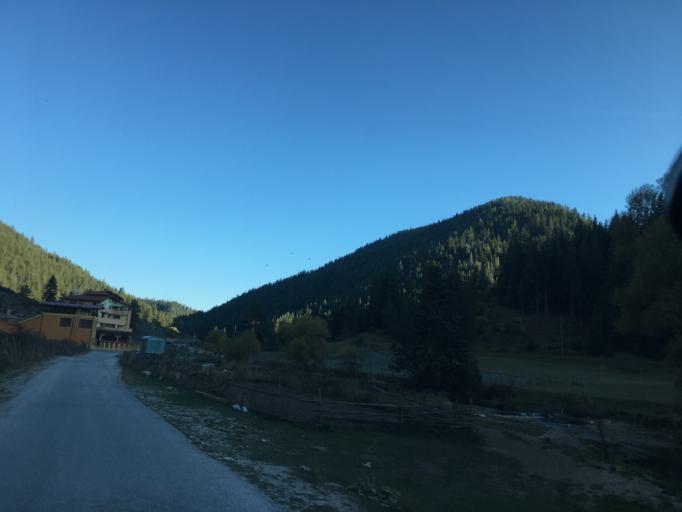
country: BG
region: Smolyan
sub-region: Obshtina Borino
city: Borino
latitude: 41.5851
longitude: 24.3911
